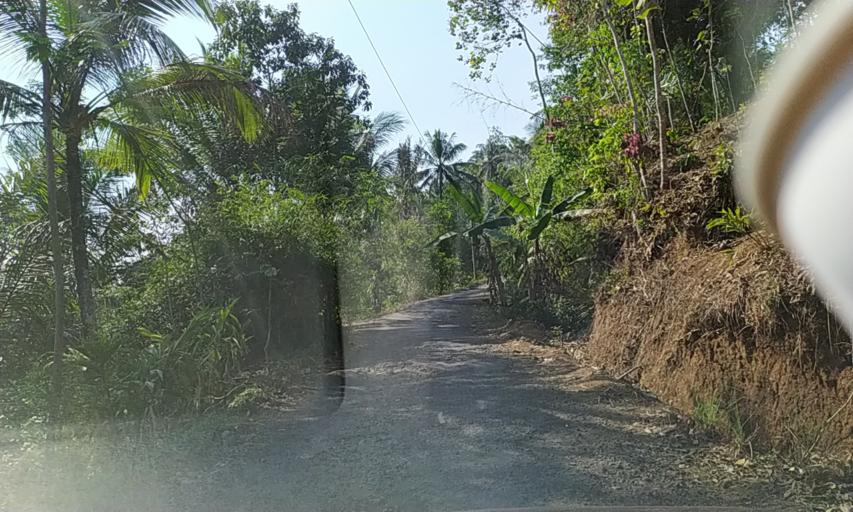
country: ID
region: Central Java
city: Datar
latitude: -7.2132
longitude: 108.6299
